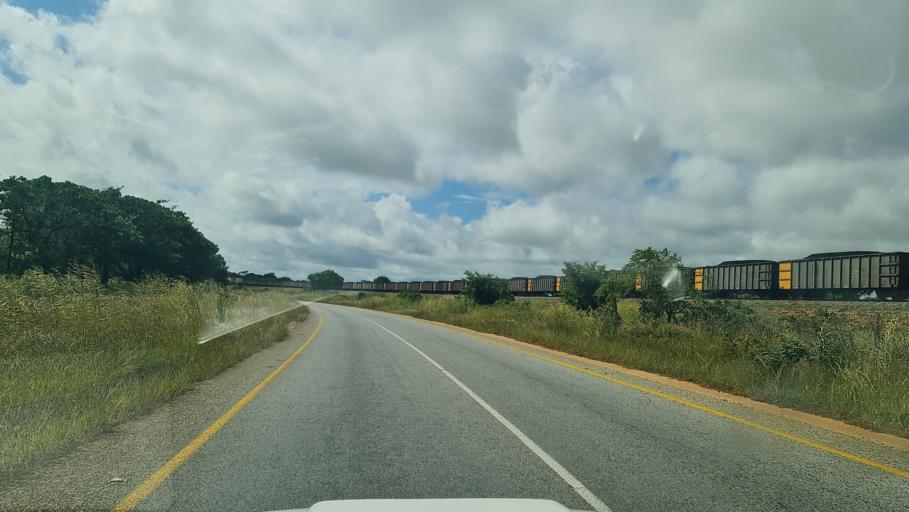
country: MZ
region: Nampula
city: Nampula
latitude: -15.0858
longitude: 39.5367
